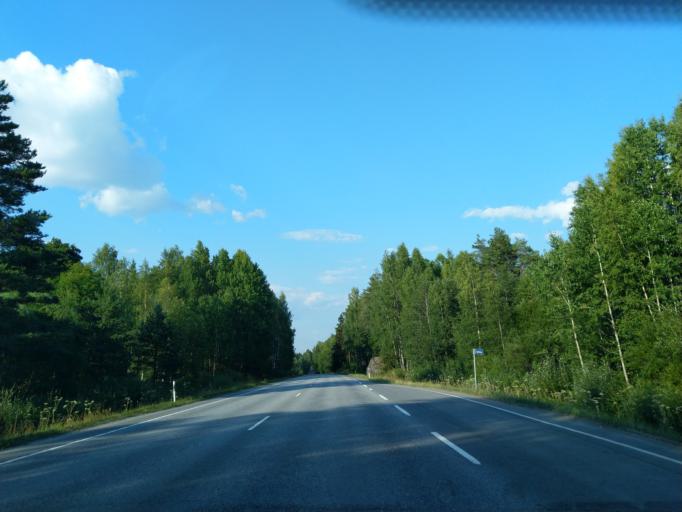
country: FI
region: Satakunta
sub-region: Pori
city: Laengelmaeki
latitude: 61.7539
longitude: 22.1255
